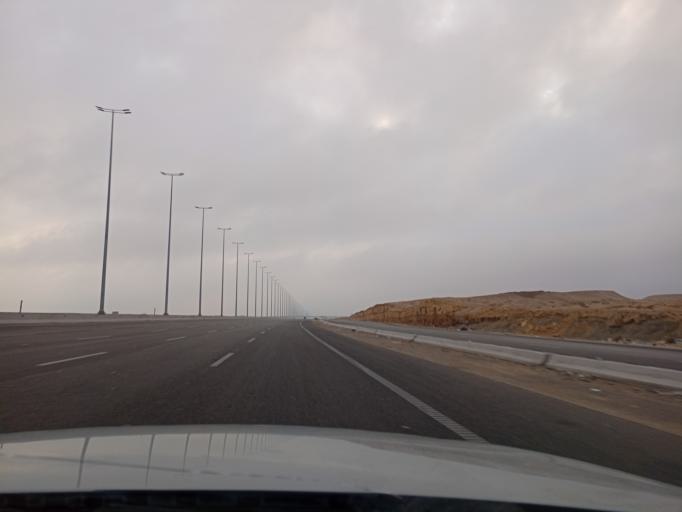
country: EG
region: Muhafazat al Qalyubiyah
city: Al Khankah
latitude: 30.0941
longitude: 31.4899
